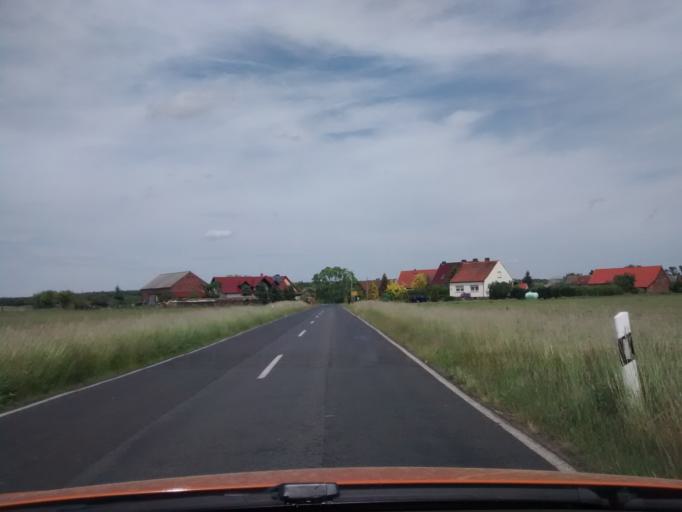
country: DE
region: Brandenburg
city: Ihlow
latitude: 51.8390
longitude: 13.2428
